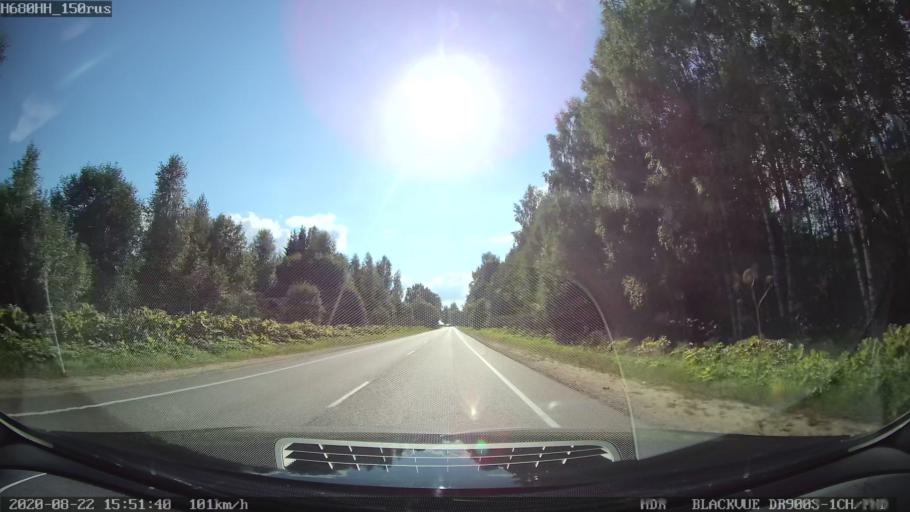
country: RU
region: Tverskaya
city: Bezhetsk
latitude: 57.6630
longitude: 36.4201
